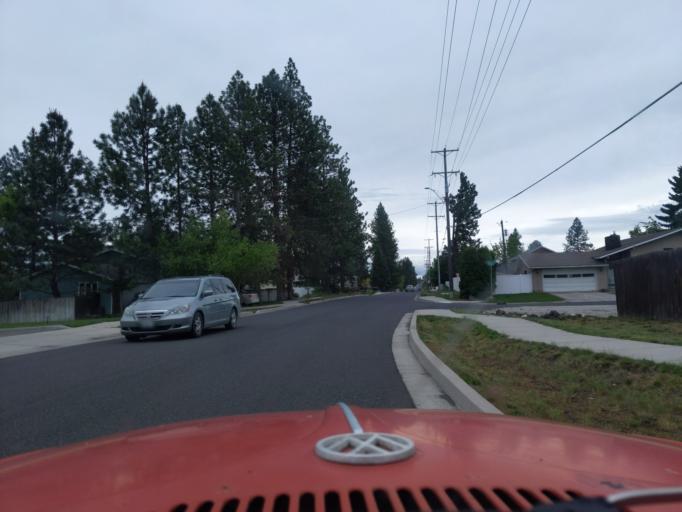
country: US
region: Washington
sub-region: Spokane County
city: Spokane
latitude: 47.6132
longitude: -117.3790
